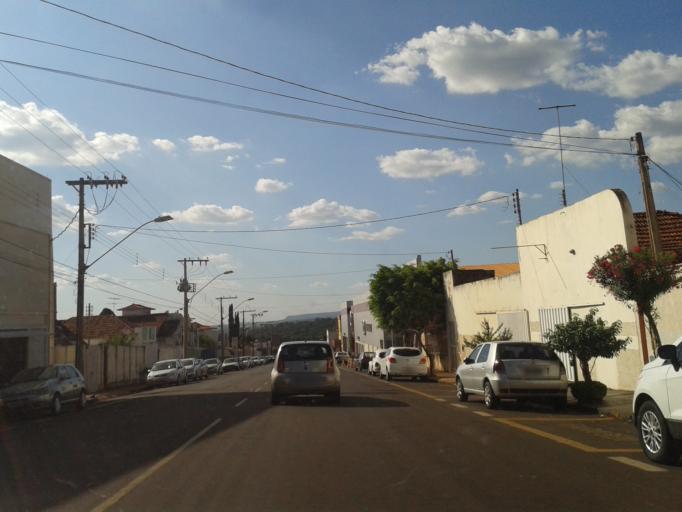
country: BR
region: Minas Gerais
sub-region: Ituiutaba
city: Ituiutaba
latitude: -18.9732
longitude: -49.4594
